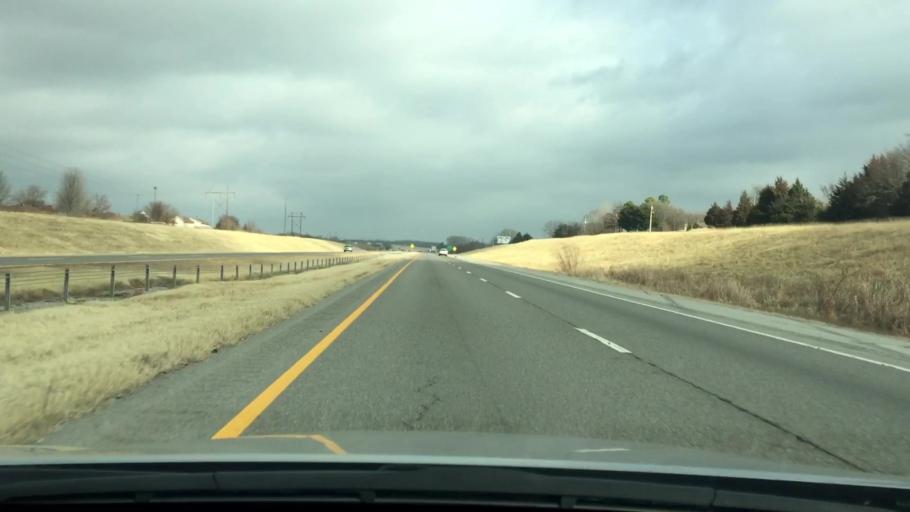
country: US
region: Oklahoma
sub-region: McClain County
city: Purcell
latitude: 35.0239
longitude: -97.3758
